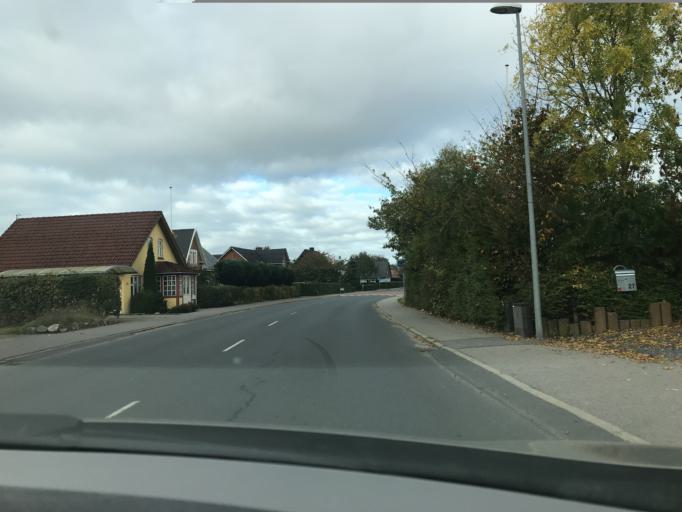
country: DK
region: South Denmark
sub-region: Kolding Kommune
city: Kolding
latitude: 55.5651
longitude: 9.4047
